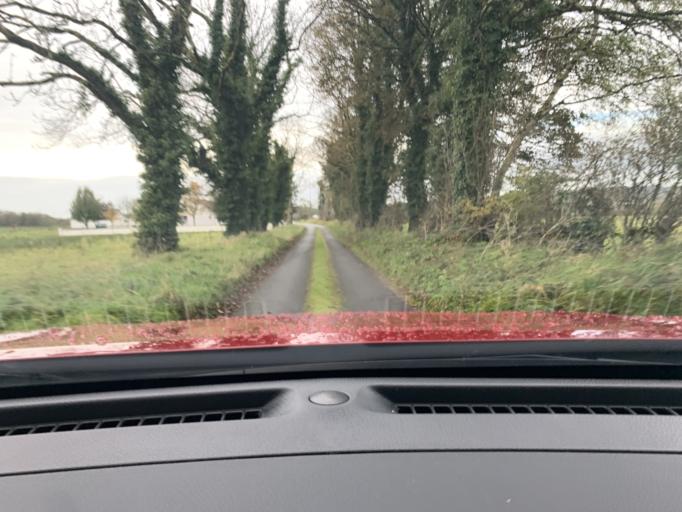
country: IE
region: Connaught
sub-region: Roscommon
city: Ballaghaderreen
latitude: 53.9114
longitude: -8.5616
